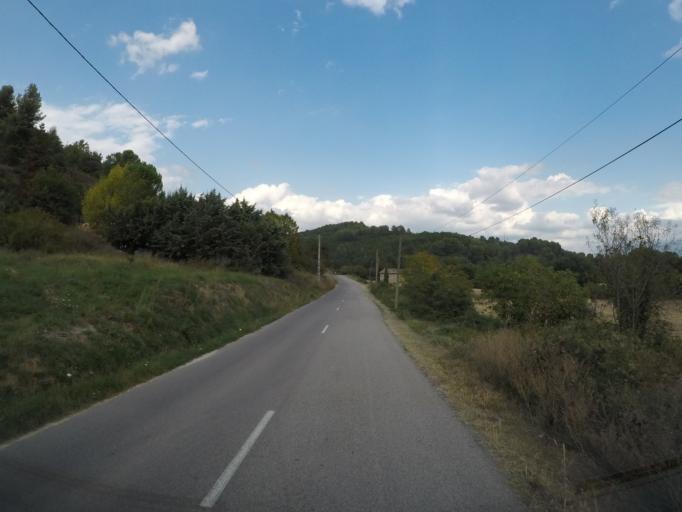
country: FR
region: Provence-Alpes-Cote d'Azur
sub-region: Departement des Alpes-de-Haute-Provence
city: Riez
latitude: 43.8150
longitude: 6.0674
